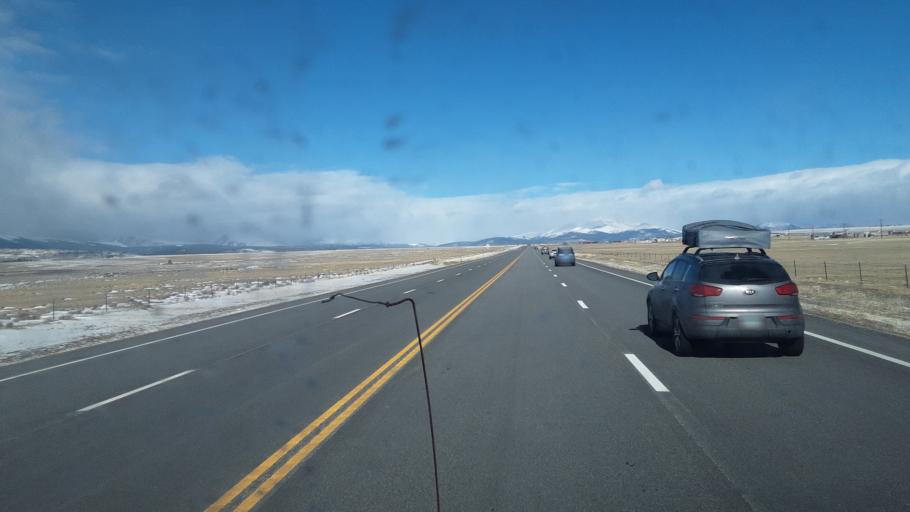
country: US
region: Colorado
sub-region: Park County
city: Fairplay
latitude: 39.1097
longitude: -105.9911
